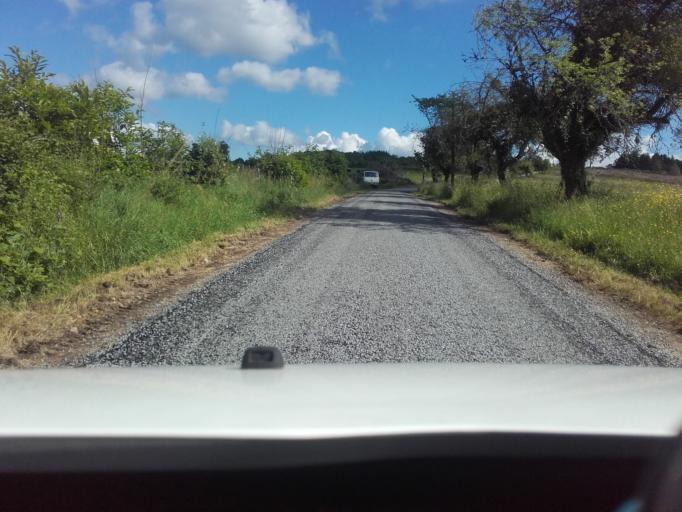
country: FR
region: Limousin
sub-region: Departement de la Correze
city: Laguenne
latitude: 45.2377
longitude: 1.8723
